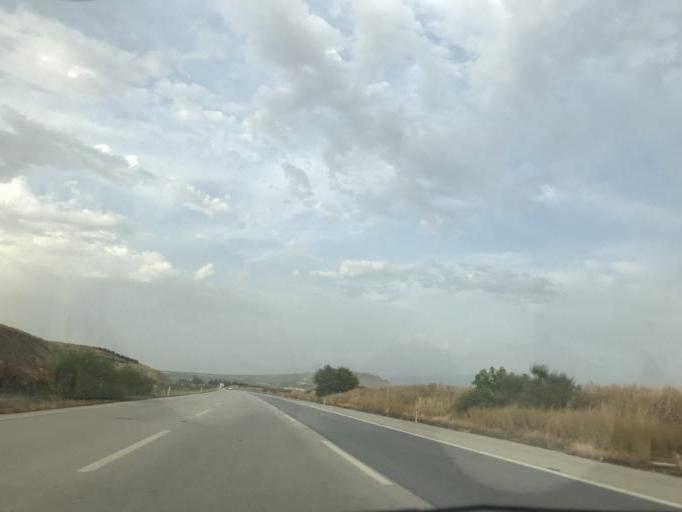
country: TR
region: Adana
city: Kosreli
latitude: 37.0144
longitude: 35.9960
